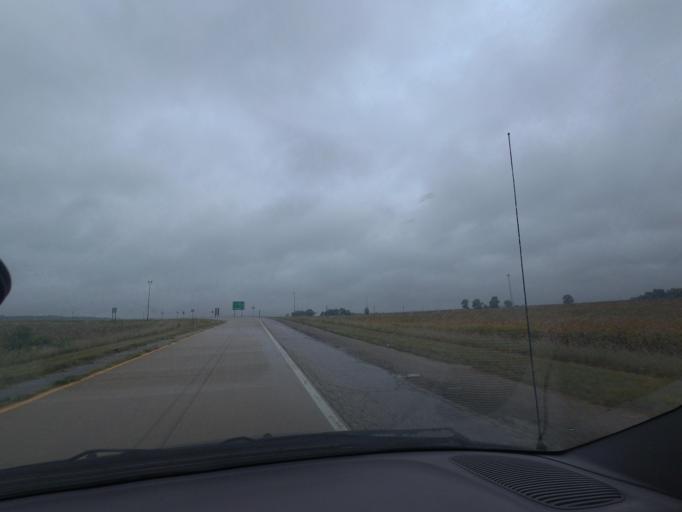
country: US
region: Illinois
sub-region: Adams County
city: Payson
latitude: 39.7180
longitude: -91.1967
